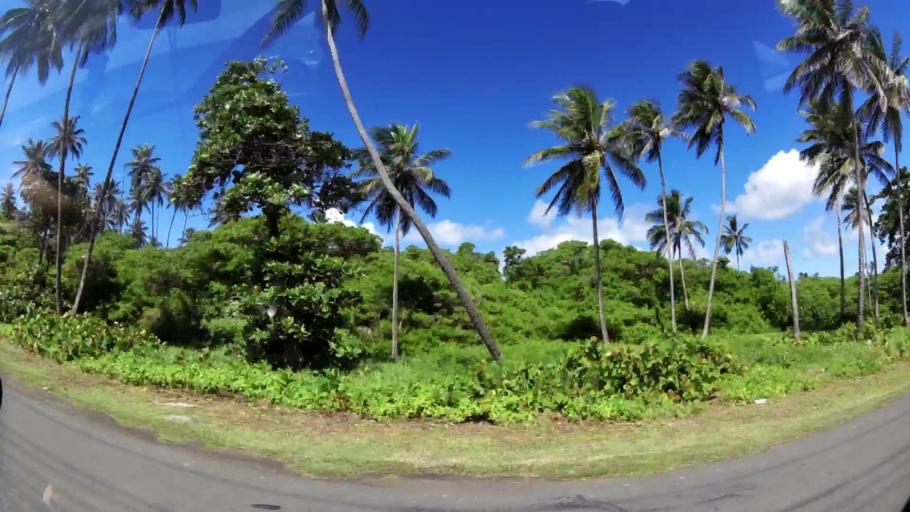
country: TT
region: Tobago
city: Scarborough
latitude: 11.1618
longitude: -60.7674
